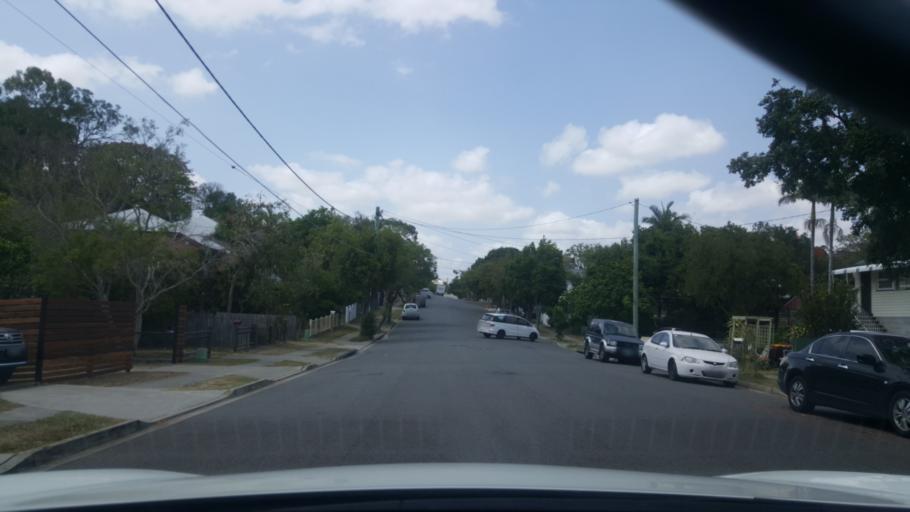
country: AU
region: Queensland
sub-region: Brisbane
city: South Brisbane
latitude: -27.4897
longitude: 153.0243
